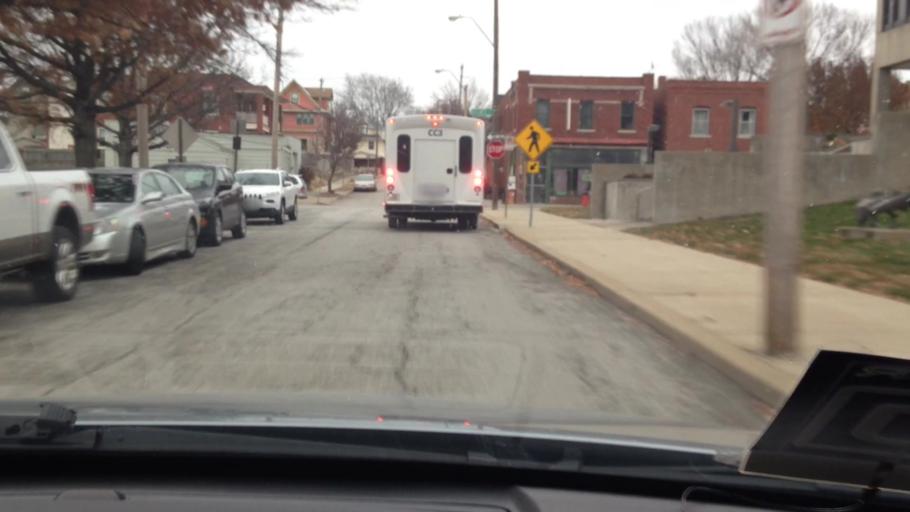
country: US
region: Missouri
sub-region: Jackson County
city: Kansas City
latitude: 39.0792
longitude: -94.5767
